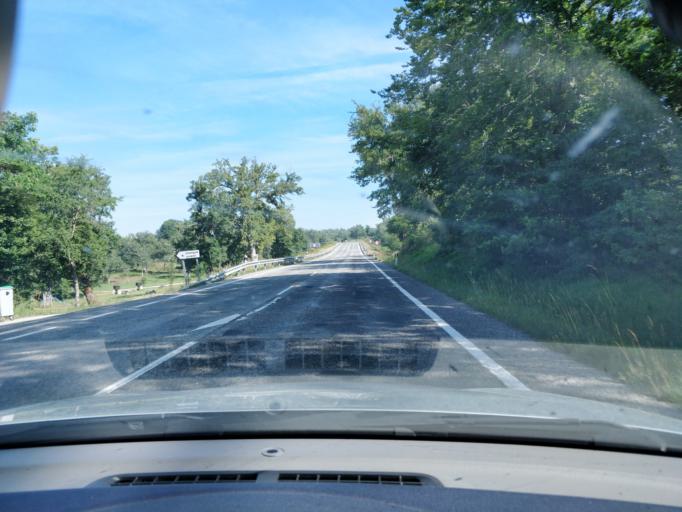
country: ES
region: Cantabria
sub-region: Provincia de Cantabria
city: San Pedro del Romeral
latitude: 42.9626
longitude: -3.7772
